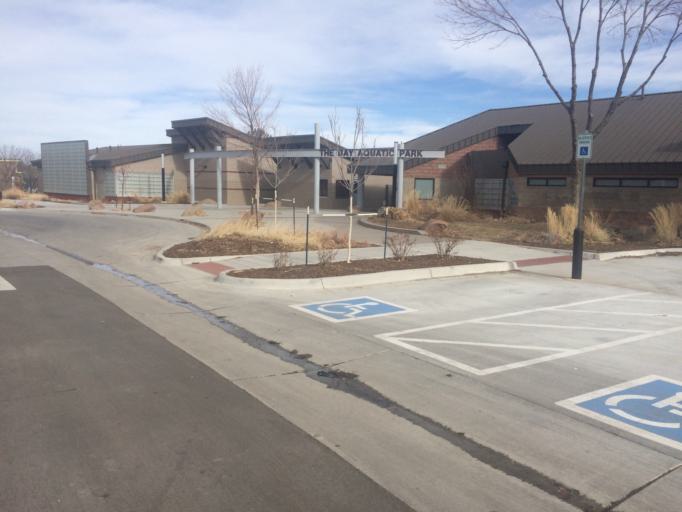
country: US
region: Colorado
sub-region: Broomfield County
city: Broomfield
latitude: 39.9193
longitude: -105.0660
